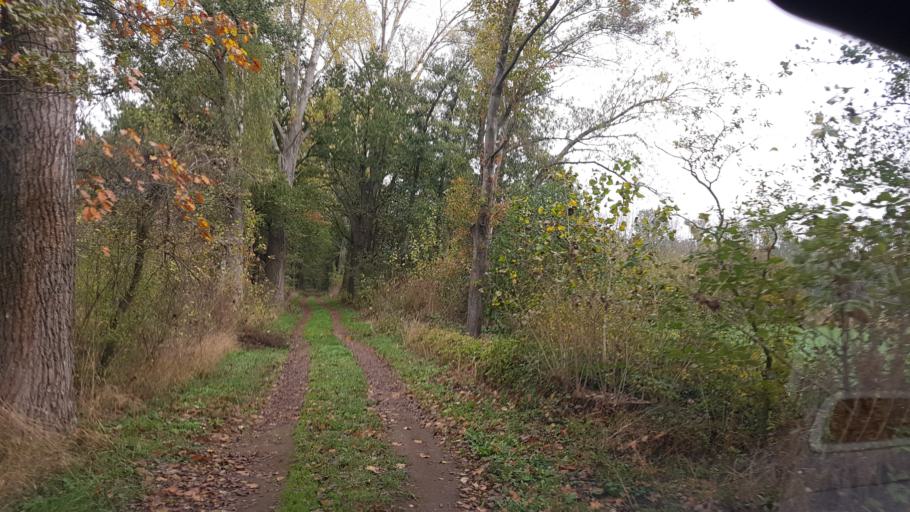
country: DE
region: Brandenburg
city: Schonewalde
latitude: 51.6918
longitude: 13.5995
